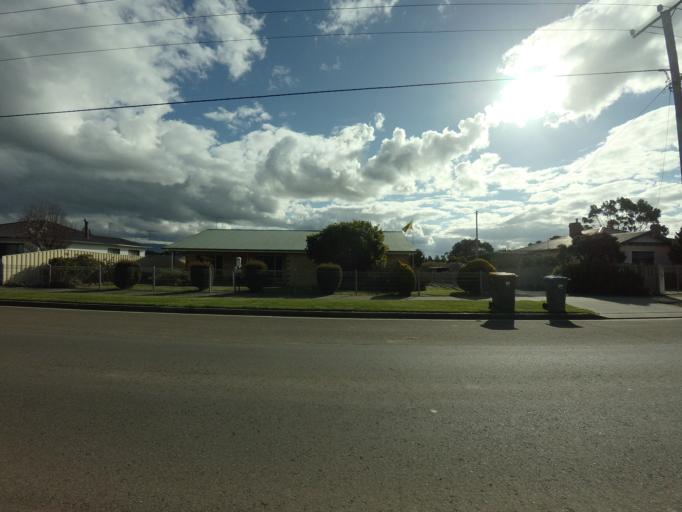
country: AU
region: Tasmania
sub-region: Northern Midlands
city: Longford
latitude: -41.6950
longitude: 147.0783
